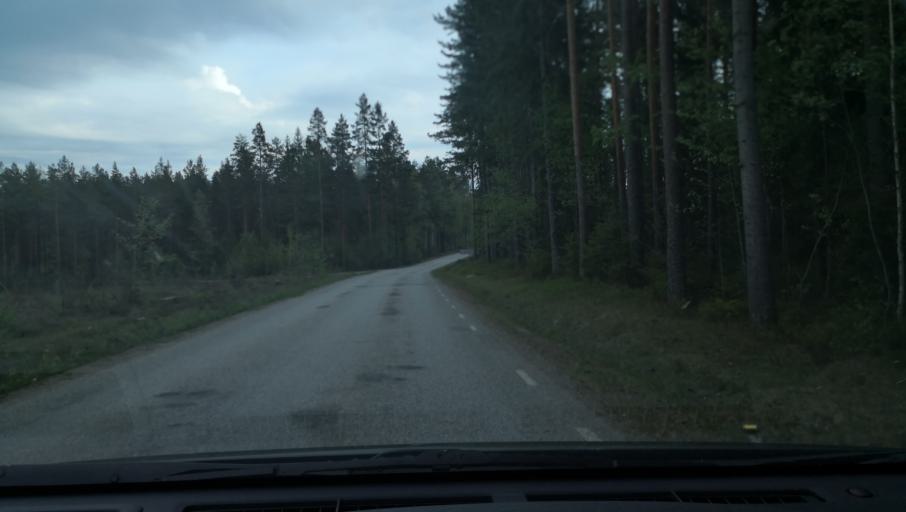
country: SE
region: Vaestmanland
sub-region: Skinnskattebergs Kommun
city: Skinnskatteberg
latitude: 59.8143
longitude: 15.5564
